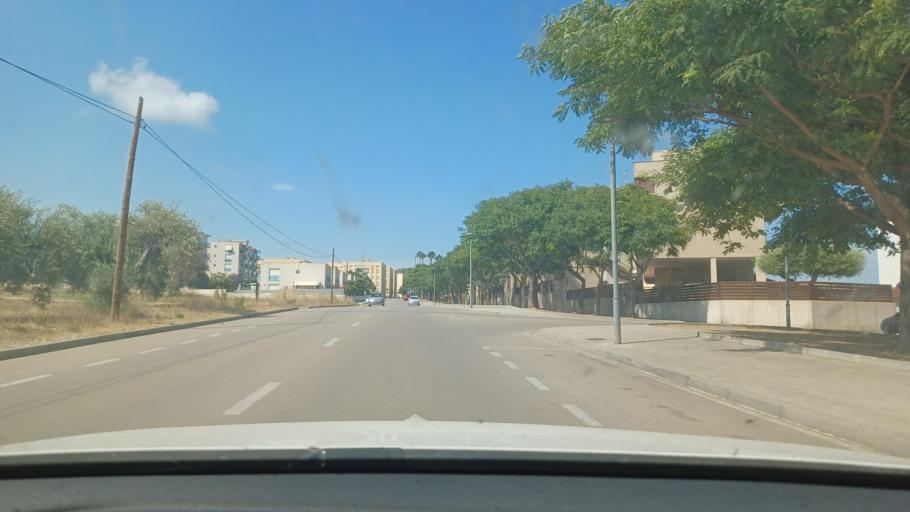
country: ES
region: Catalonia
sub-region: Provincia de Tarragona
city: Sant Carles de la Rapita
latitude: 40.6123
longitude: 0.5830
